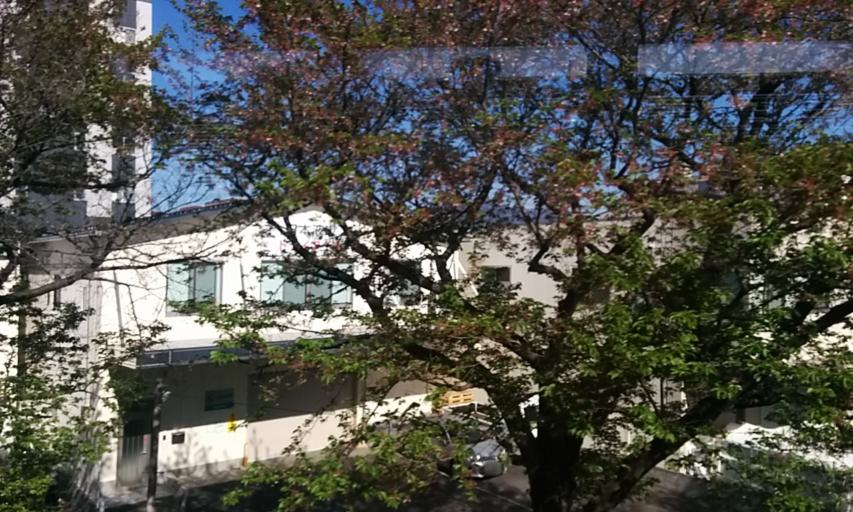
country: JP
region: Kyoto
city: Muko
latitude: 34.9949
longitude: 135.7218
